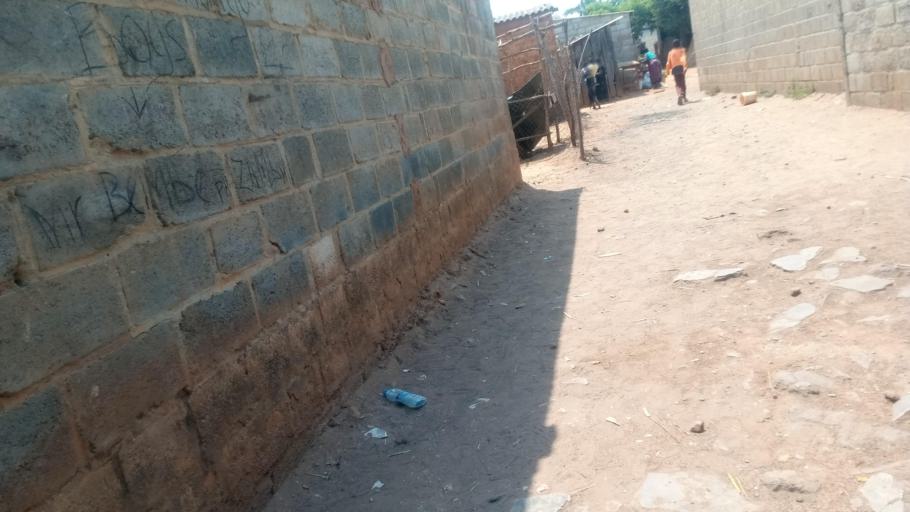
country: ZM
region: Lusaka
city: Lusaka
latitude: -15.4454
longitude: 28.3853
